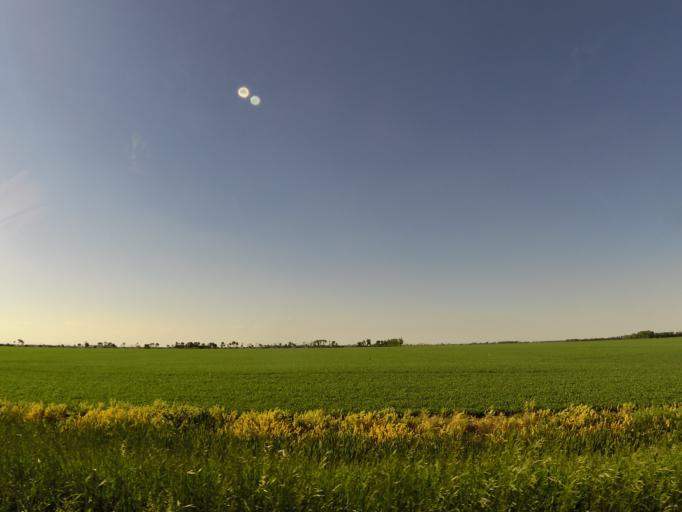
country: US
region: North Dakota
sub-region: Walsh County
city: Grafton
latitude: 48.3977
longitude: -97.2456
